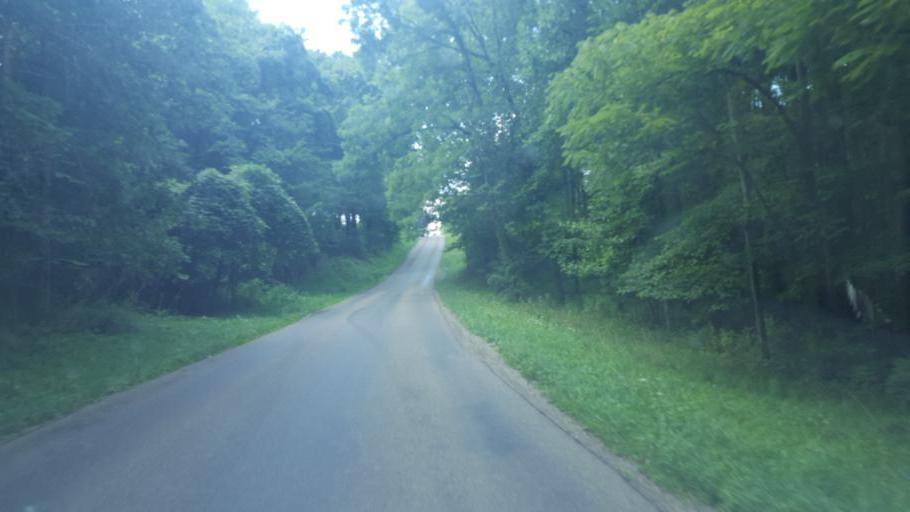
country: US
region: Ohio
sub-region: Knox County
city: Mount Vernon
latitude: 40.4249
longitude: -82.4710
